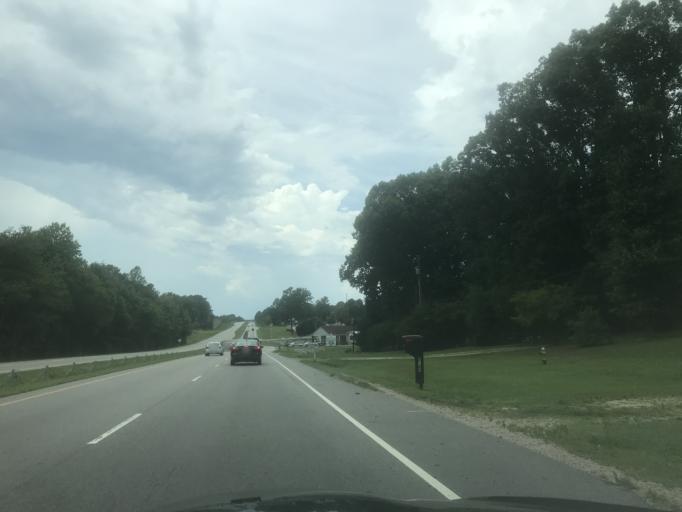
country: US
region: North Carolina
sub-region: Wake County
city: Garner
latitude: 35.6836
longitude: -78.5376
